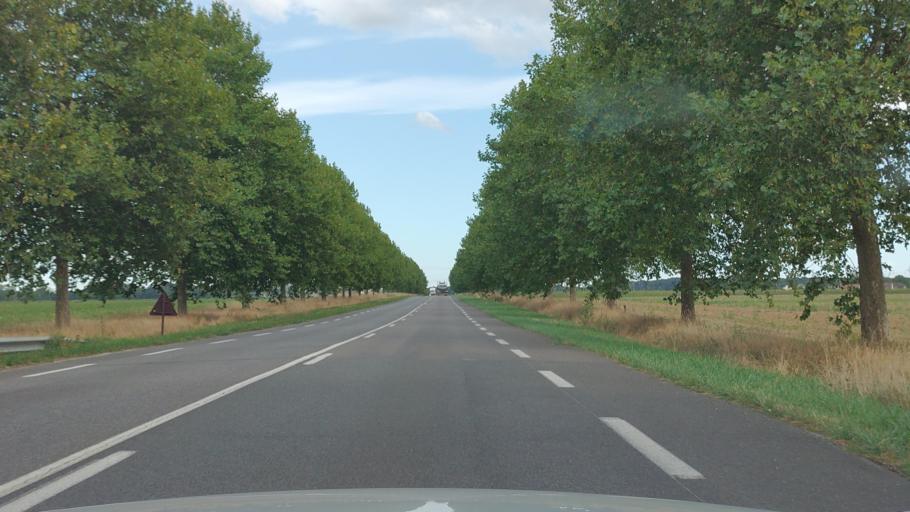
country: FR
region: Ile-de-France
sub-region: Departement de Seine-et-Marne
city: Moisenay
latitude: 48.5486
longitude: 2.7560
